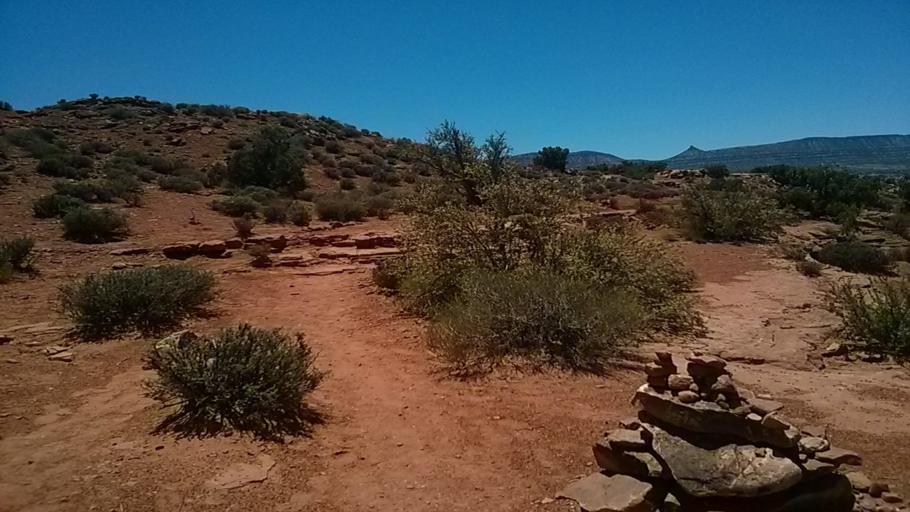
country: US
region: Arizona
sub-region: Coconino County
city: Page
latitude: 37.4774
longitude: -111.2191
